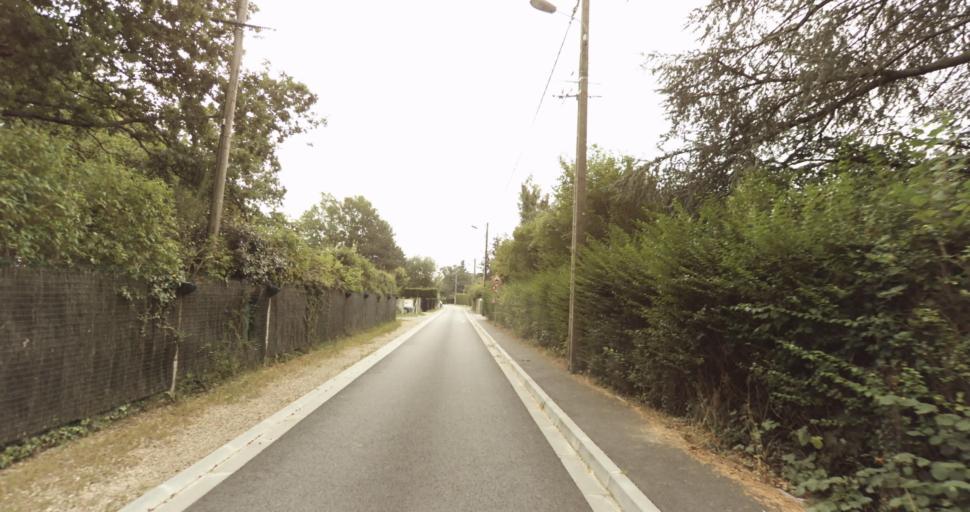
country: FR
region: Haute-Normandie
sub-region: Departement de l'Eure
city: Marcilly-sur-Eure
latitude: 48.8342
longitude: 1.3105
